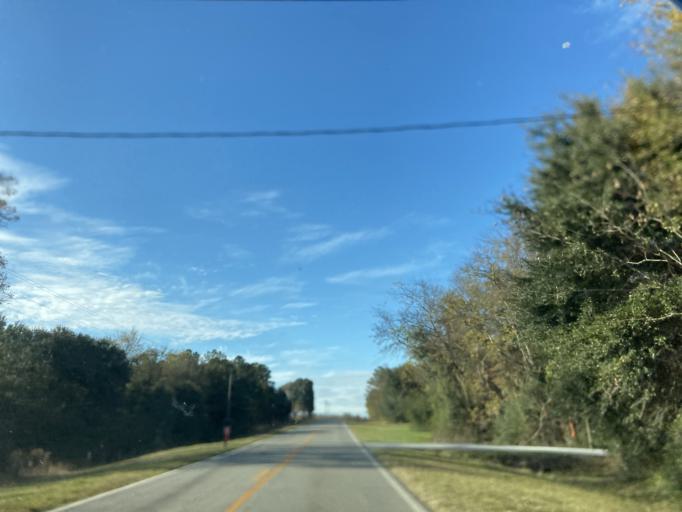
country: US
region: Georgia
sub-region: Jones County
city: Gray
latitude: 32.8928
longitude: -83.5086
